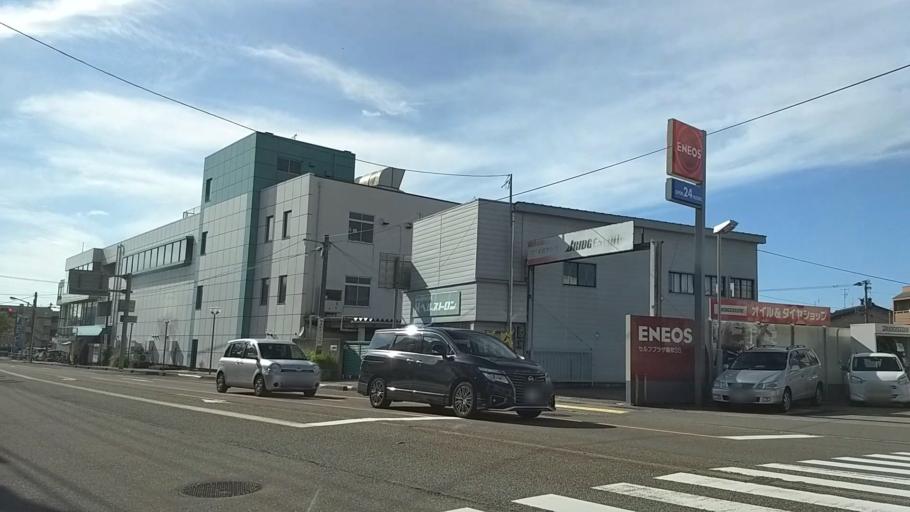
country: JP
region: Ishikawa
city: Kanazawa-shi
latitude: 36.5844
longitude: 136.6732
